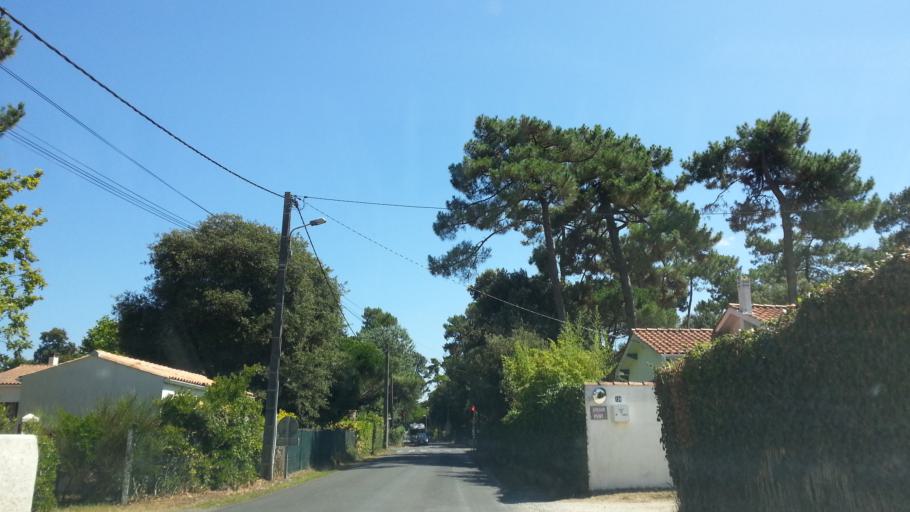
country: FR
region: Poitou-Charentes
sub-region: Departement de la Charente-Maritime
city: Dolus-d'Oleron
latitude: 45.8821
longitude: -1.2549
